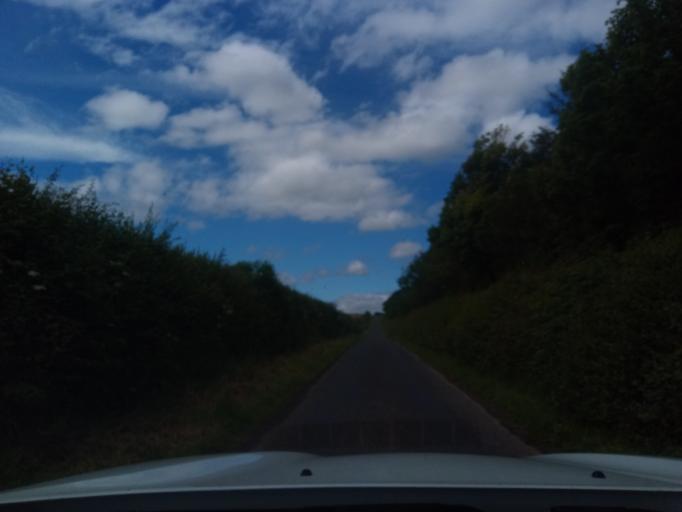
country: GB
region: Scotland
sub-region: The Scottish Borders
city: Jedburgh
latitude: 55.5635
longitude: -2.5407
